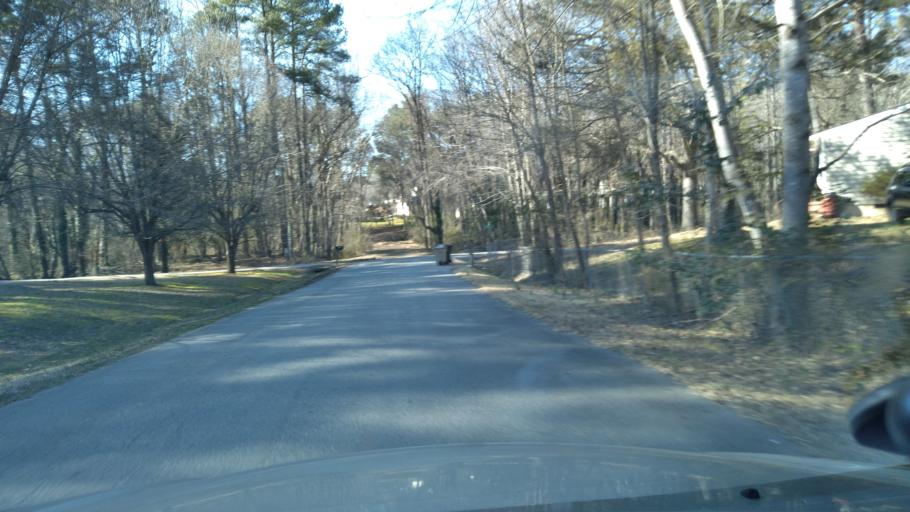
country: US
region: North Carolina
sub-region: Wake County
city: Garner
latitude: 35.6979
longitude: -78.6361
